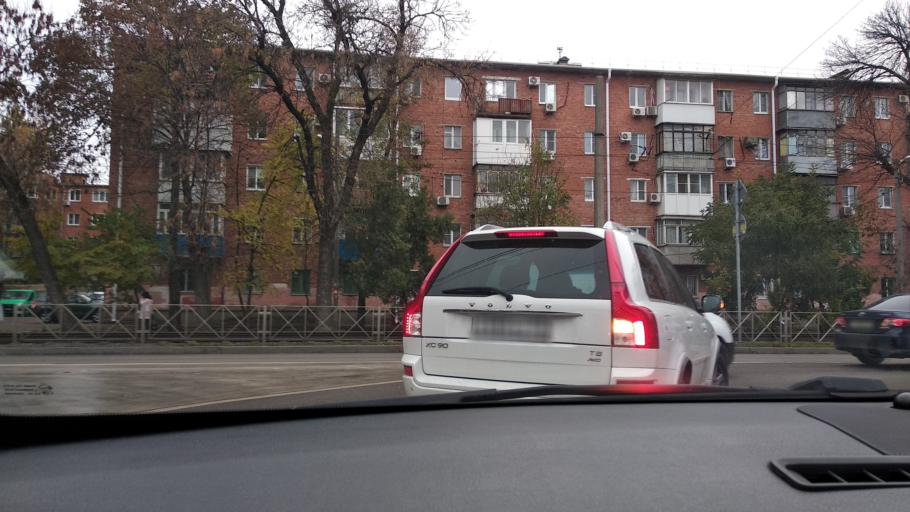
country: RU
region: Krasnodarskiy
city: Krasnodar
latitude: 45.0430
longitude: 38.9812
